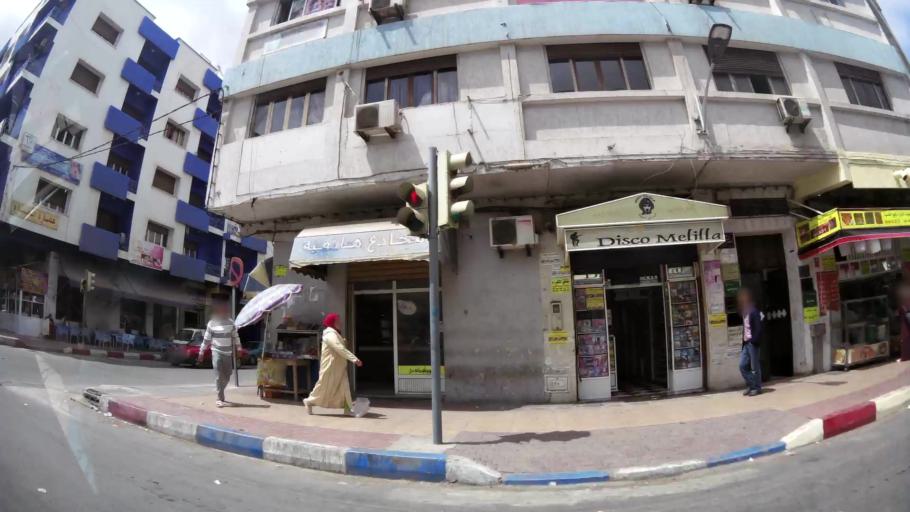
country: MA
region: Oriental
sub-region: Nador
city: Nador
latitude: 35.1768
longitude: -2.9279
